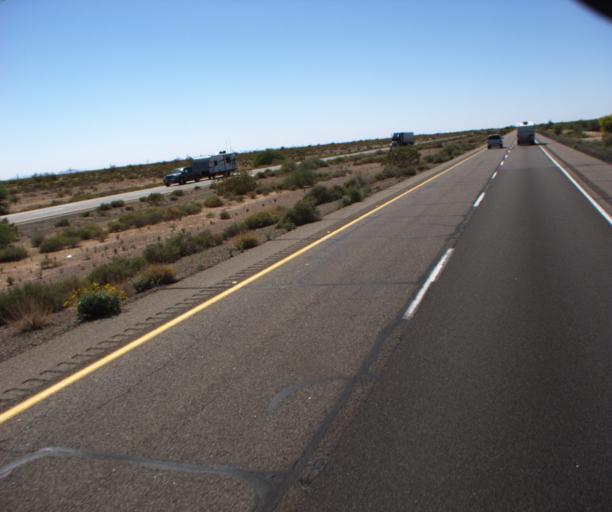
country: US
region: Arizona
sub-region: Maricopa County
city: Gila Bend
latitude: 32.9053
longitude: -112.9899
